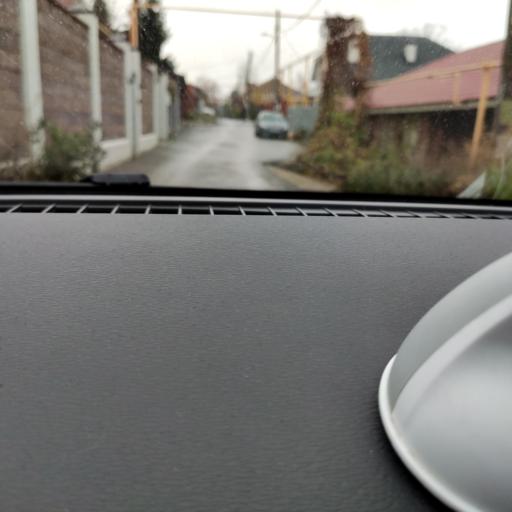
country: RU
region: Samara
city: Samara
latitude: 53.2730
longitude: 50.2099
